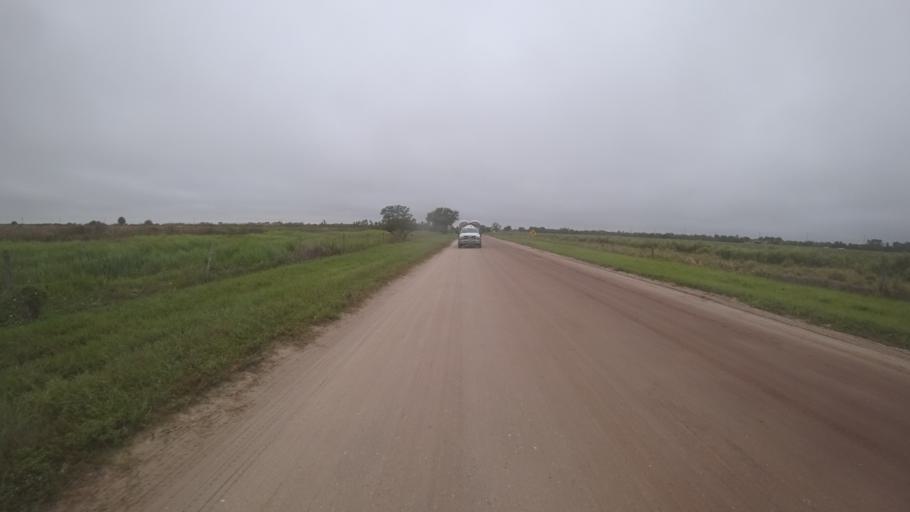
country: US
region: Florida
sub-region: Sarasota County
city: The Meadows
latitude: 27.4671
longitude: -82.3376
